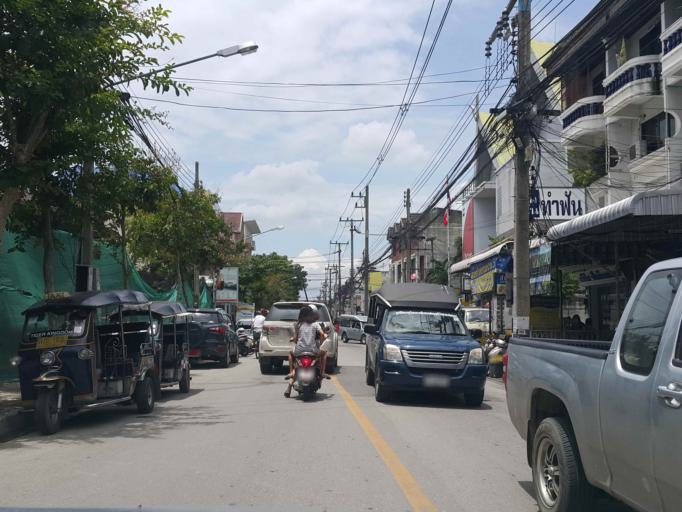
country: TH
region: Chiang Mai
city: Chiang Mai
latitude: 18.7860
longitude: 98.9821
